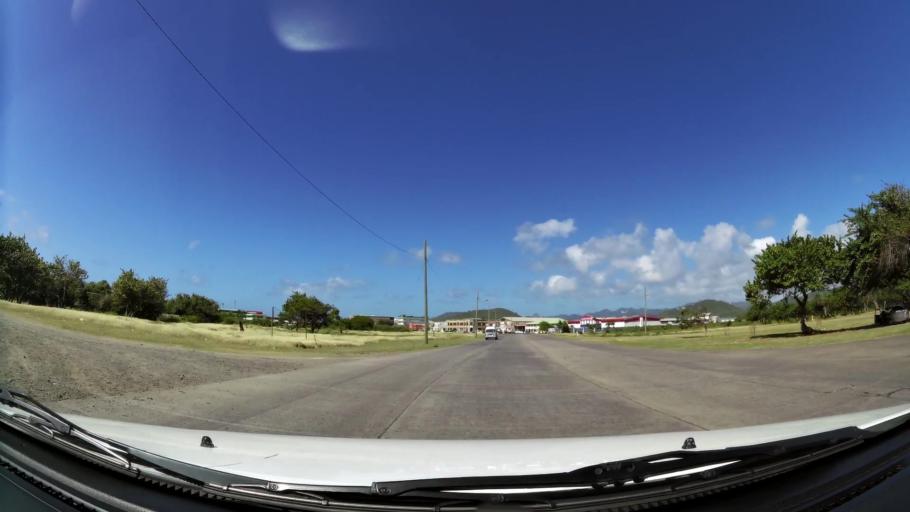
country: LC
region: Vieux-Fort
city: Vieux Fort
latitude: 13.7285
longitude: -60.9463
